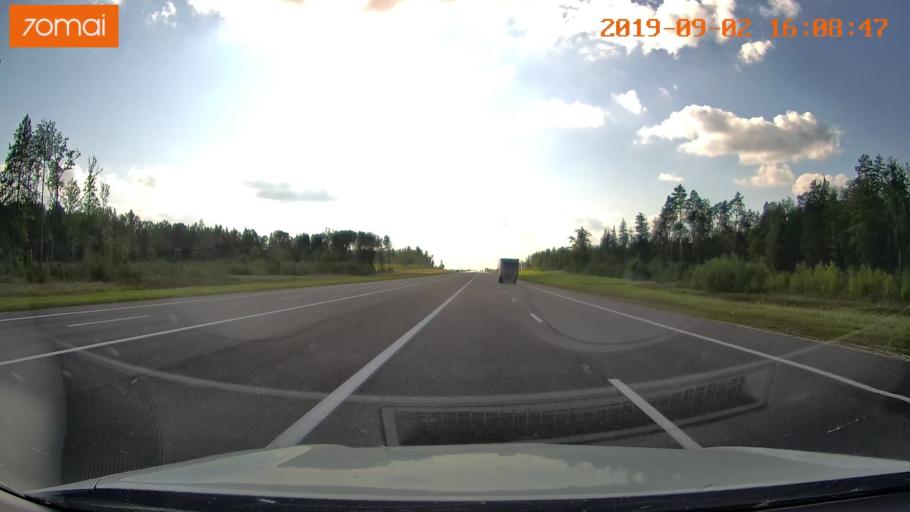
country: BY
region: Minsk
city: Byerazino
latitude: 53.7731
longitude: 28.7200
